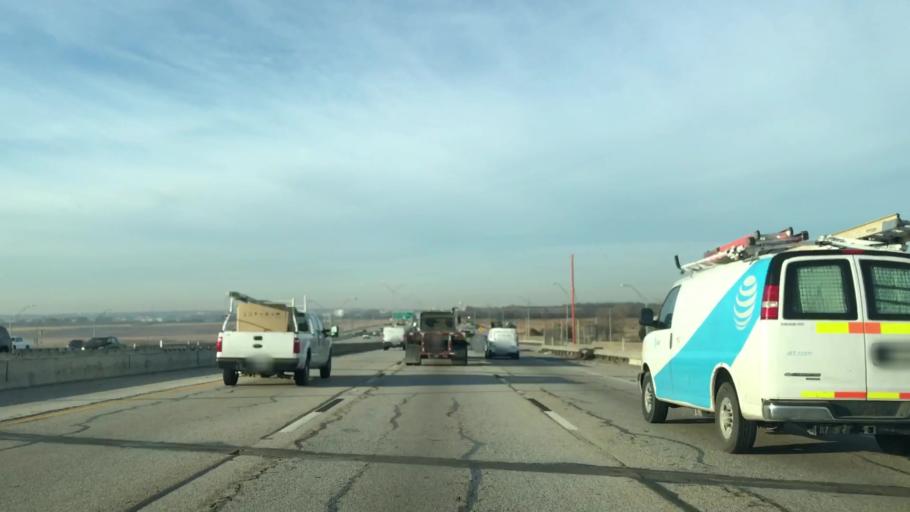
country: US
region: Texas
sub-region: Tarrant County
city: Saginaw
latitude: 32.8367
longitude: -97.3630
